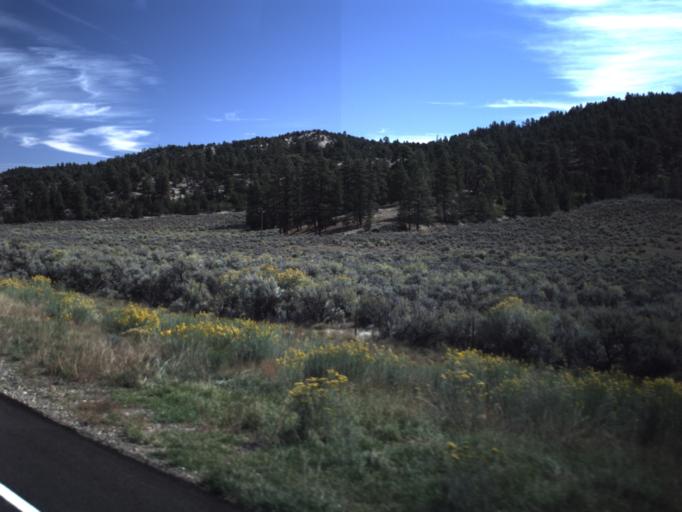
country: US
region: Utah
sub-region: Garfield County
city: Panguitch
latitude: 37.6571
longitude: -111.8367
